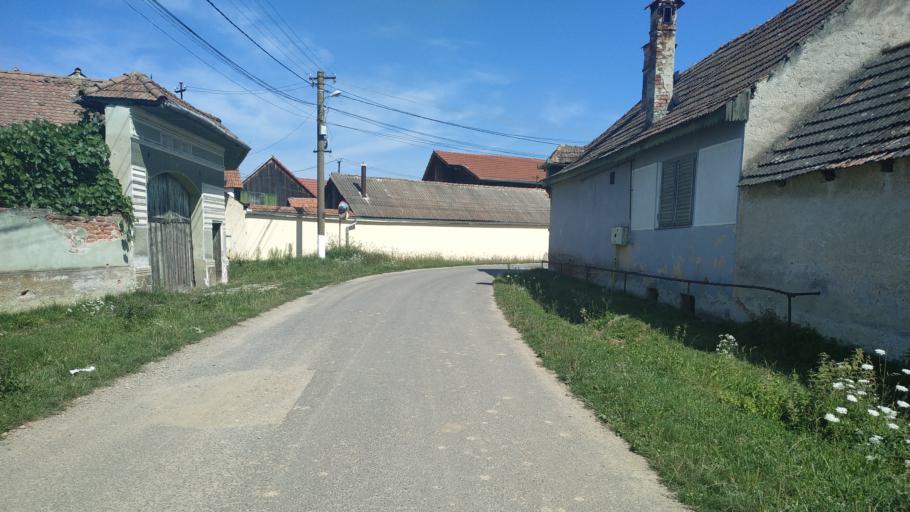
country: RO
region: Brasov
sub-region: Comuna Beclean
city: Beclean
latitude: 45.8262
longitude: 24.9262
